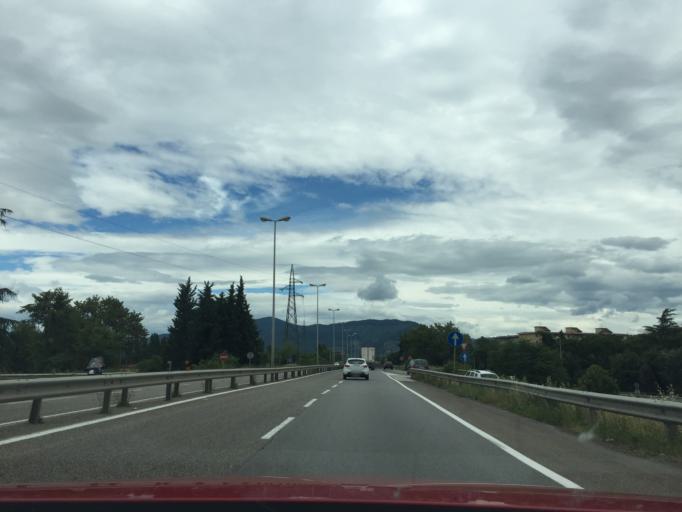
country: IT
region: Tuscany
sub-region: Province of Florence
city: Mantignano-Ugnano
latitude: 43.7807
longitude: 11.1863
